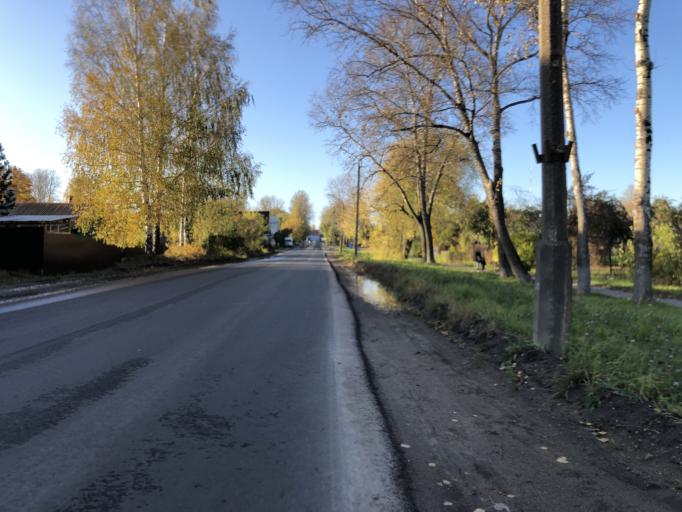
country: RU
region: Tverskaya
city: Rzhev
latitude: 56.2438
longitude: 34.3429
